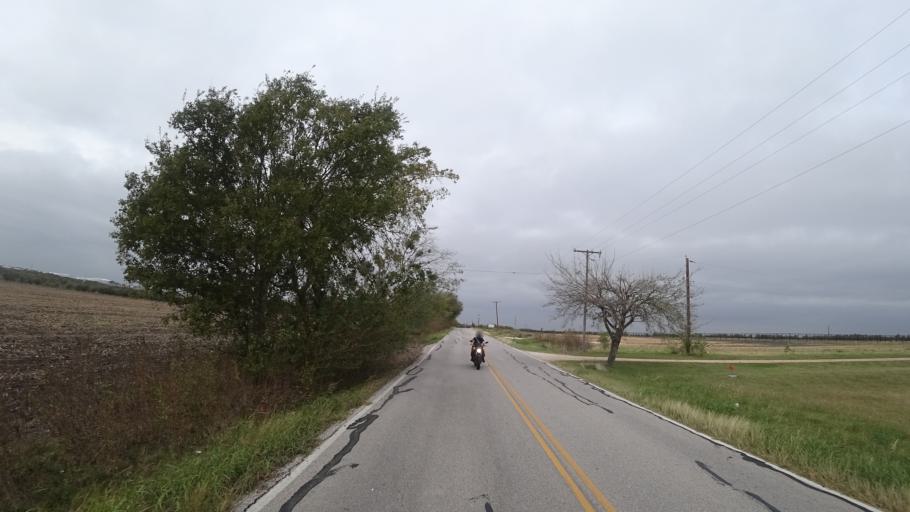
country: US
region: Texas
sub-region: Travis County
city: Manor
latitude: 30.4057
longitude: -97.5563
